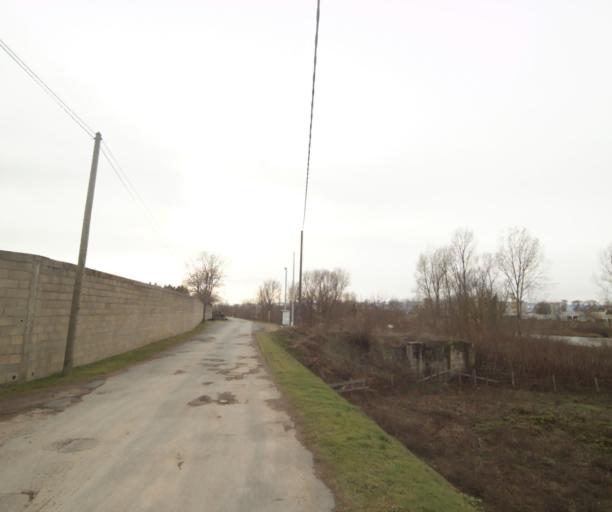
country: FR
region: Rhone-Alpes
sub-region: Departement de la Loire
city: Le Coteau
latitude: 46.0415
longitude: 4.0905
